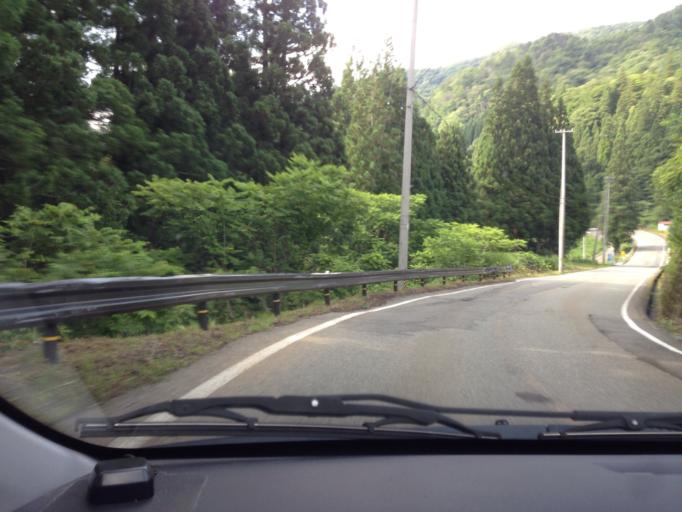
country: JP
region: Fukushima
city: Kitakata
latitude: 37.4263
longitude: 139.5387
